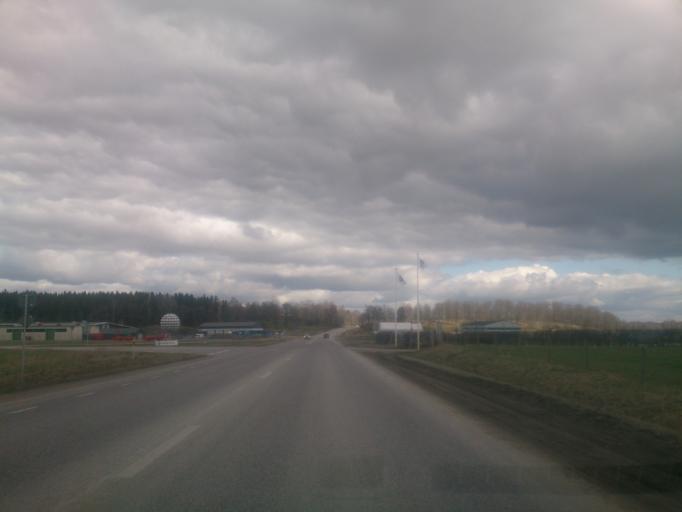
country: SE
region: OEstergoetland
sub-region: Norrkopings Kommun
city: Norrkoping
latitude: 58.5648
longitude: 16.0803
